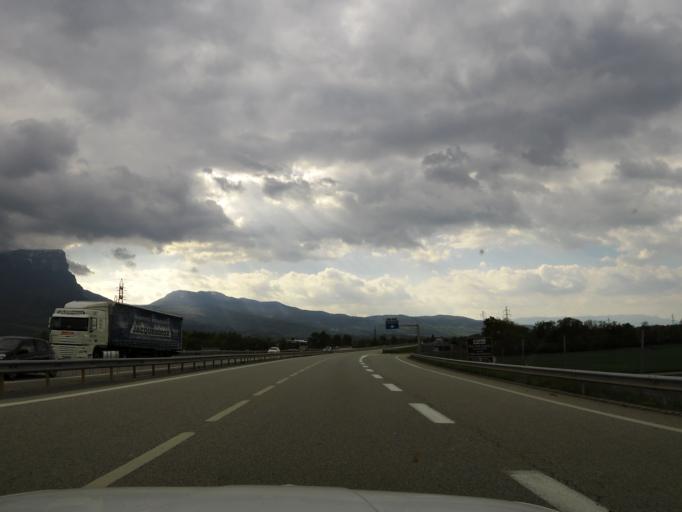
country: FR
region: Rhone-Alpes
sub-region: Departement de la Savoie
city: Montmelian
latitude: 45.4823
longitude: 6.0302
